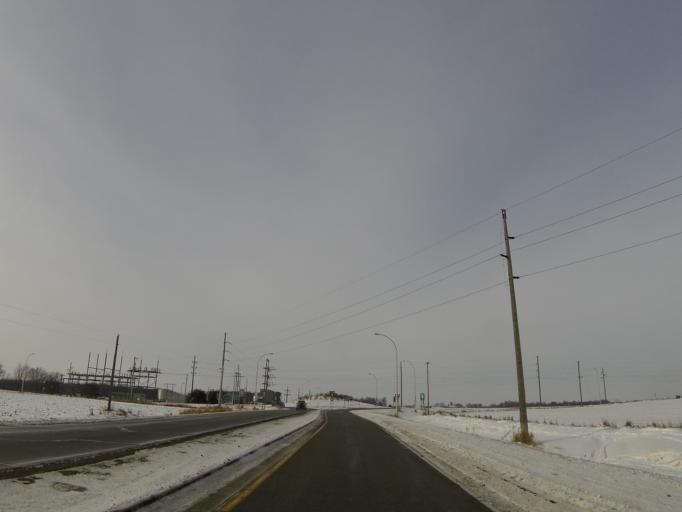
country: US
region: Minnesota
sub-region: Carver County
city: Waconia
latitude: 44.9055
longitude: -93.8168
